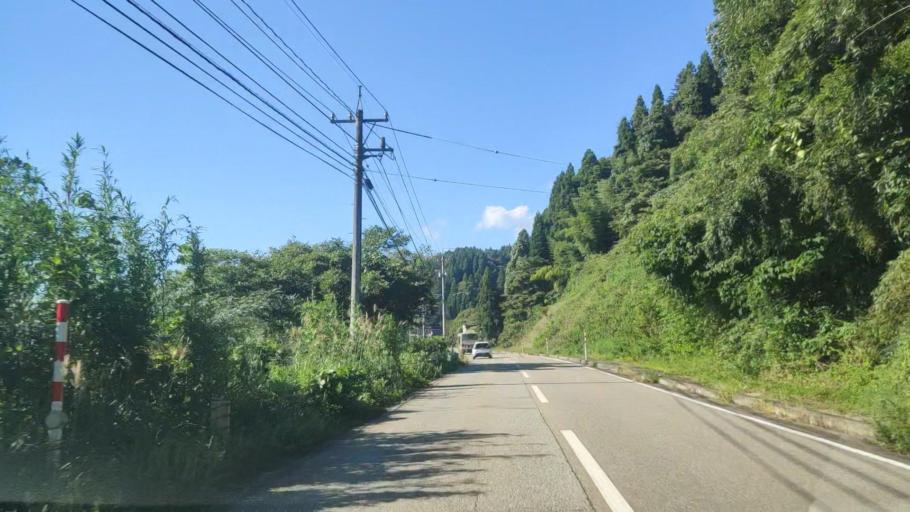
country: JP
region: Ishikawa
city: Nanao
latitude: 37.2754
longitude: 137.0539
